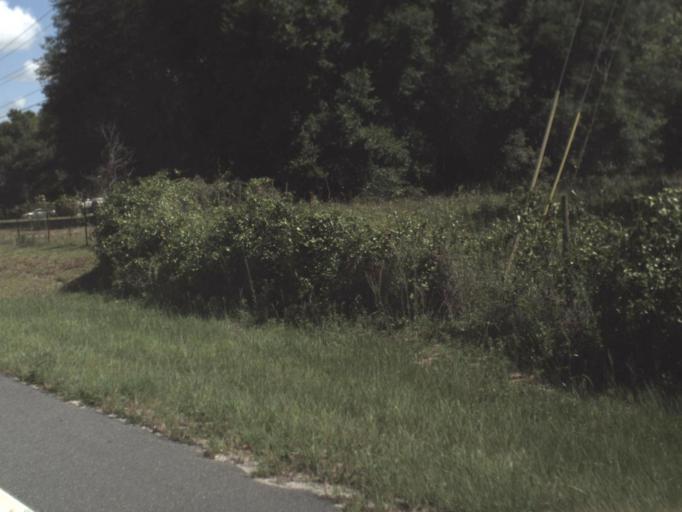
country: US
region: Florida
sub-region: Clay County
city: Keystone Heights
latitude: 29.7303
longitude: -81.9563
